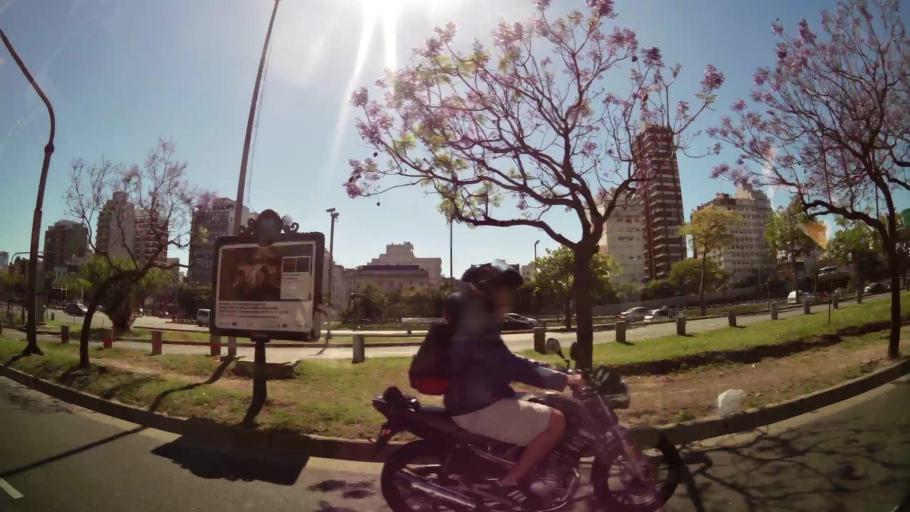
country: AR
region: Buenos Aires F.D.
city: Buenos Aires
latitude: -34.6203
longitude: -58.3814
